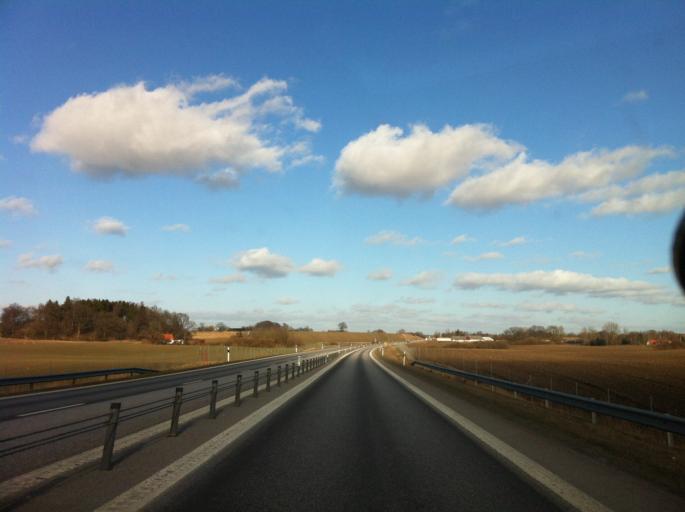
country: SE
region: Skane
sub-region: Svedala Kommun
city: Svedala
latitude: 55.4800
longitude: 13.2185
